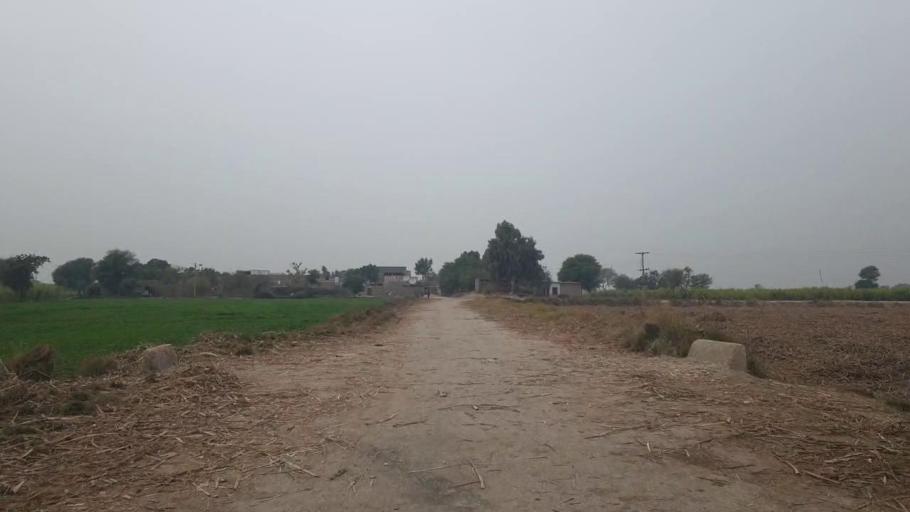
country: PK
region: Sindh
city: Shahdadpur
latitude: 25.8654
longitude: 68.6141
